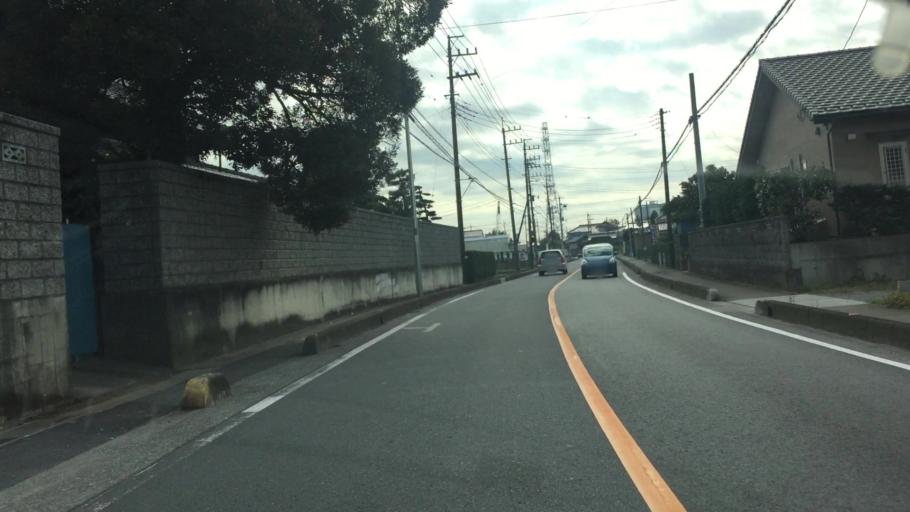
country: JP
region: Saitama
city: Yoshikawa
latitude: 35.8695
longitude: 139.8652
